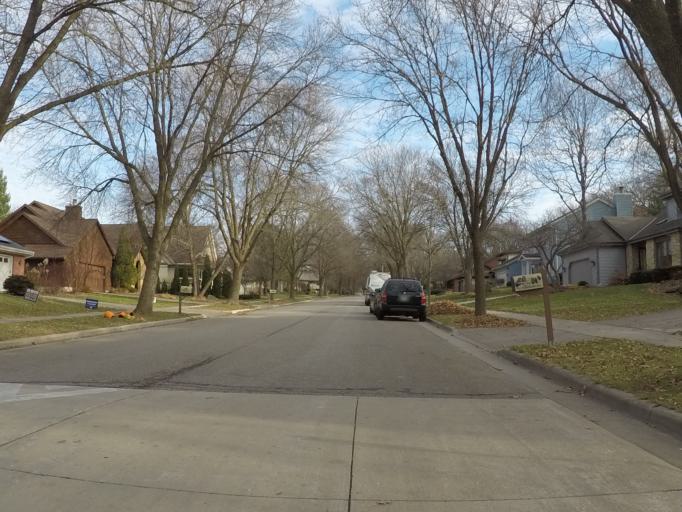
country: US
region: Wisconsin
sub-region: Dane County
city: Middleton
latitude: 43.0718
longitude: -89.5145
